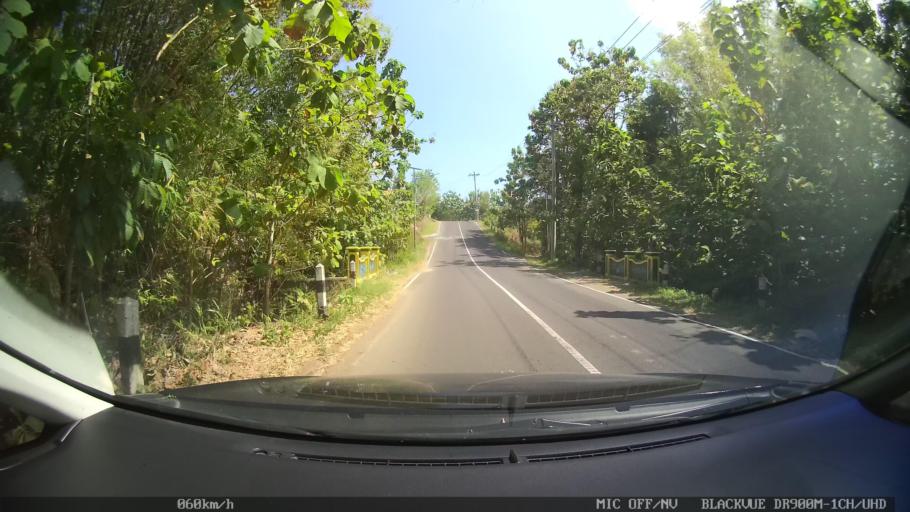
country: ID
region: Daerah Istimewa Yogyakarta
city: Pundong
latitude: -7.9730
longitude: 110.3489
